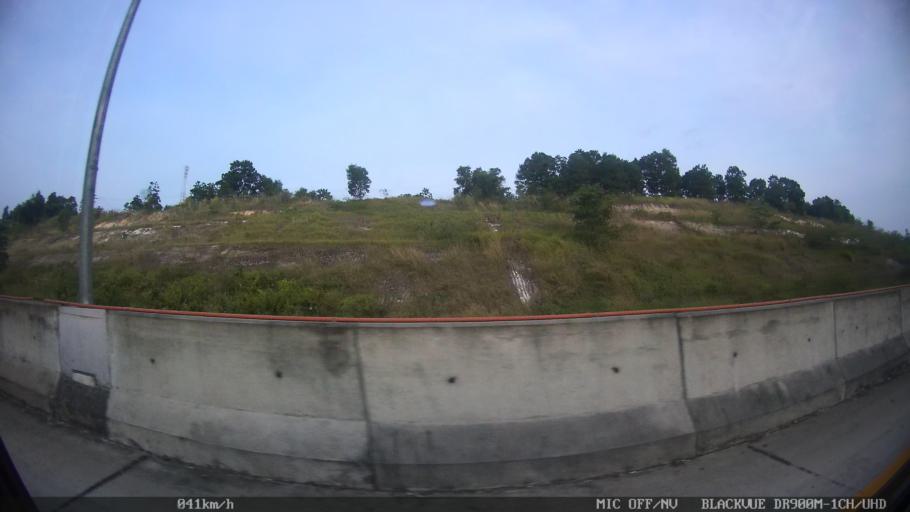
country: ID
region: Lampung
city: Penengahan
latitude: -5.8412
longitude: 105.7286
